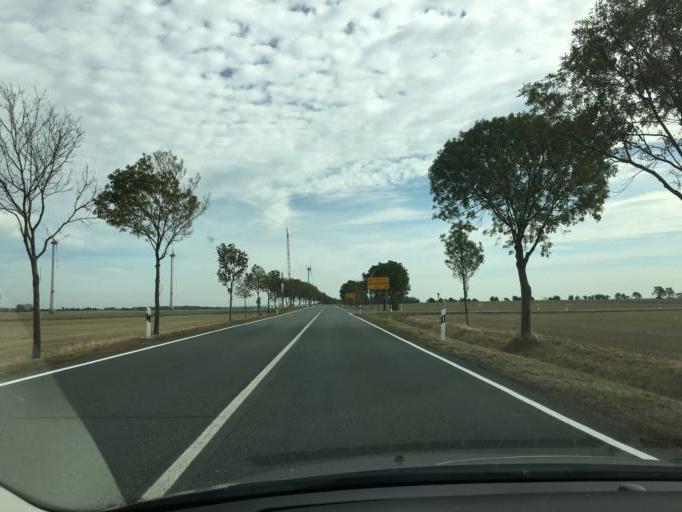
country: DE
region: Saxony
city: Stauchitz
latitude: 51.2788
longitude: 13.1916
